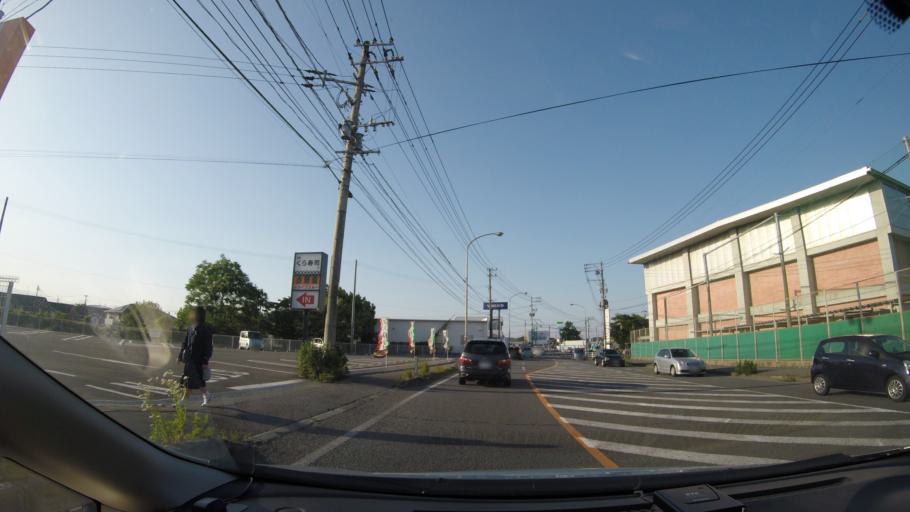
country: JP
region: Oita
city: Oita
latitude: 33.2064
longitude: 131.6034
